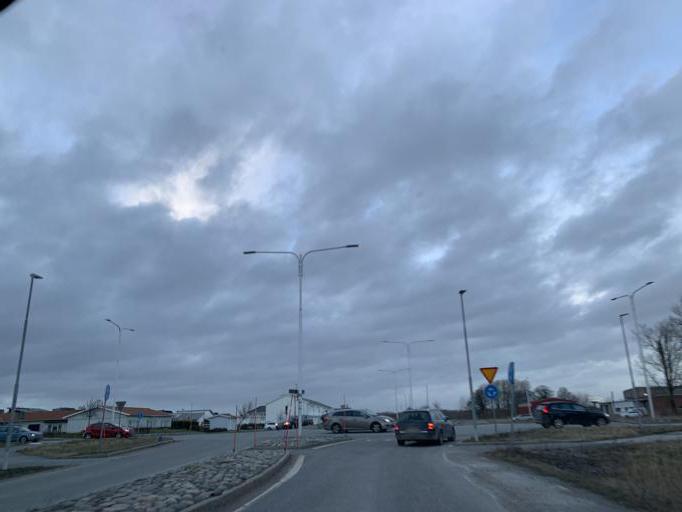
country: SE
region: OErebro
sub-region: Orebro Kommun
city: Orebro
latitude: 59.2613
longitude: 15.2609
